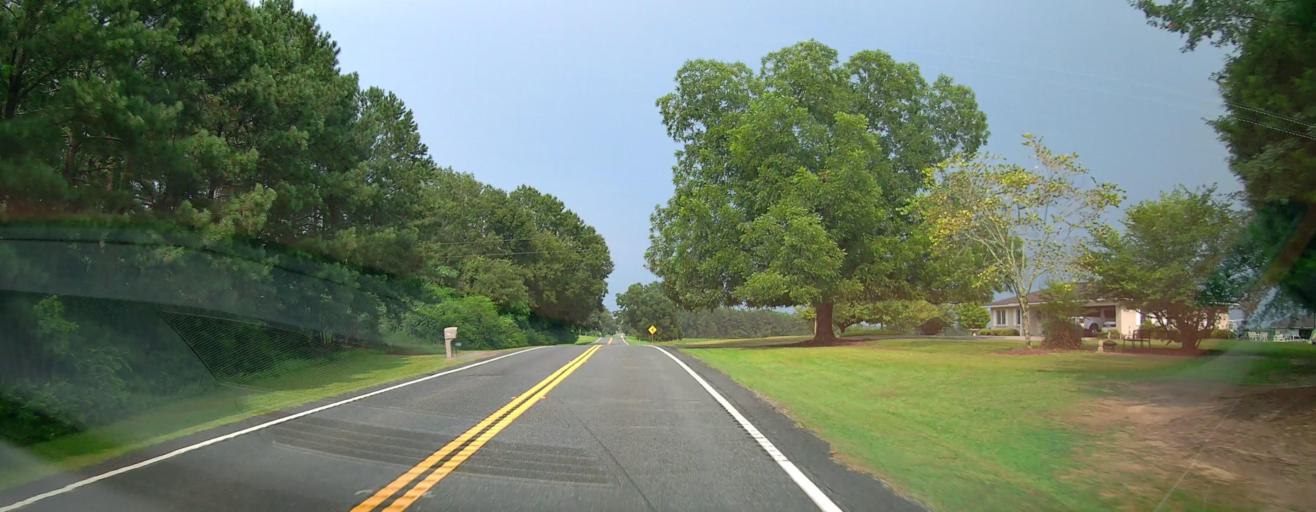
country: US
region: Georgia
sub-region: Twiggs County
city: Jeffersonville
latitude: 32.5926
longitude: -83.3470
